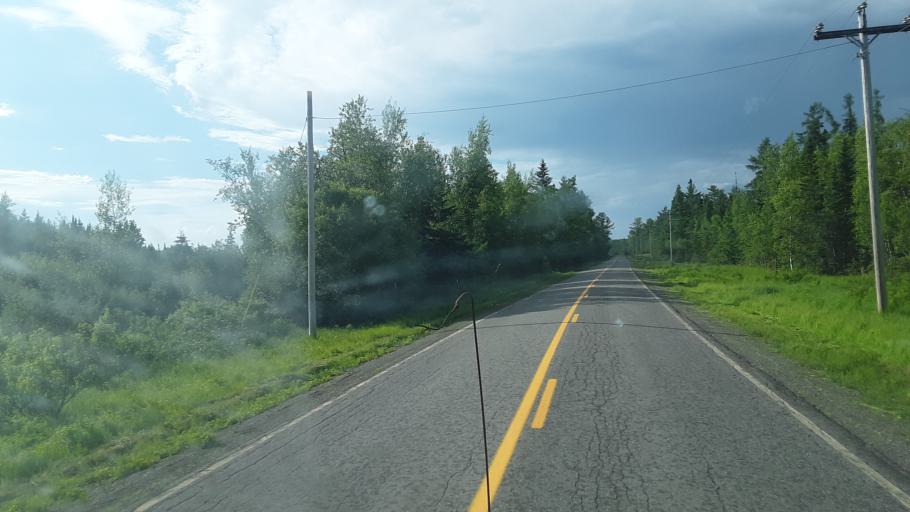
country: US
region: Maine
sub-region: Washington County
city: Calais
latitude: 45.1842
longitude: -67.5185
